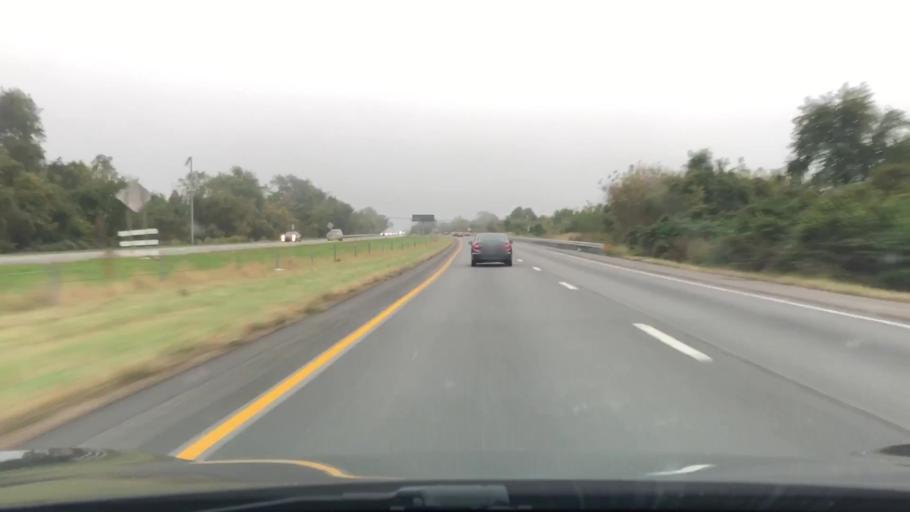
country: US
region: Pennsylvania
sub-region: Bucks County
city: Woodside
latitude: 40.2245
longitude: -74.8815
